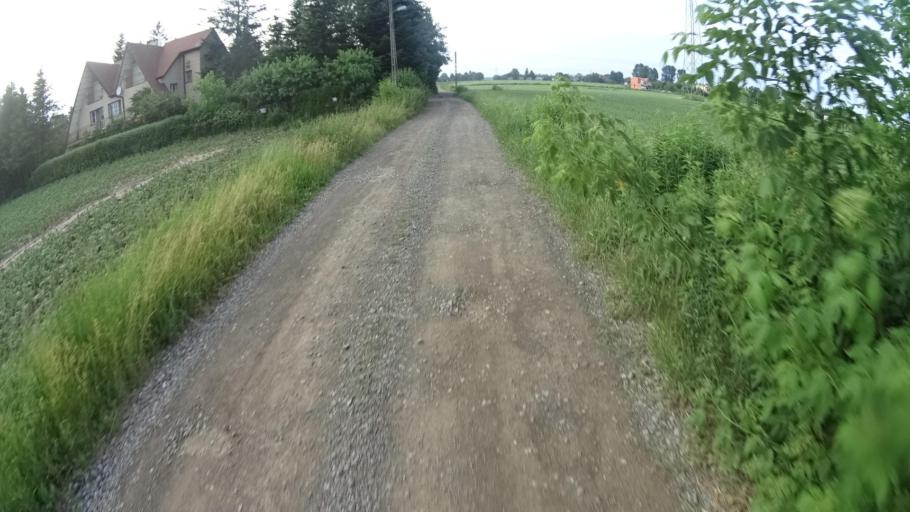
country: PL
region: Masovian Voivodeship
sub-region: Powiat warszawski zachodni
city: Babice
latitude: 52.2200
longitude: 20.8548
